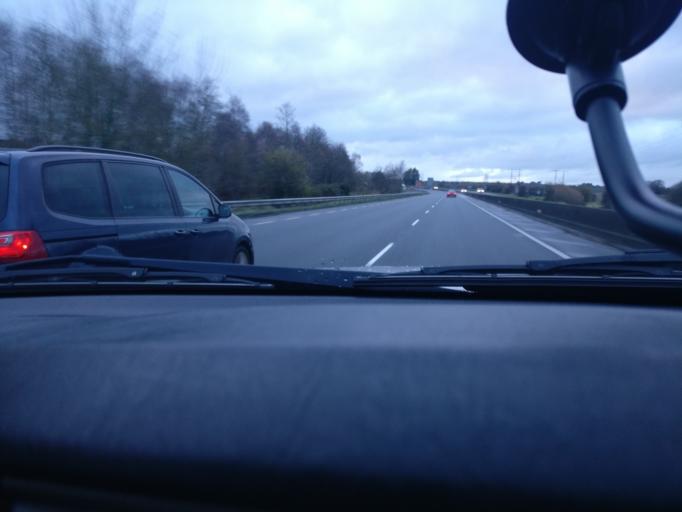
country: IE
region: Leinster
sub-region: An Iarmhi
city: Athlone
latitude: 53.4348
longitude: -7.9463
